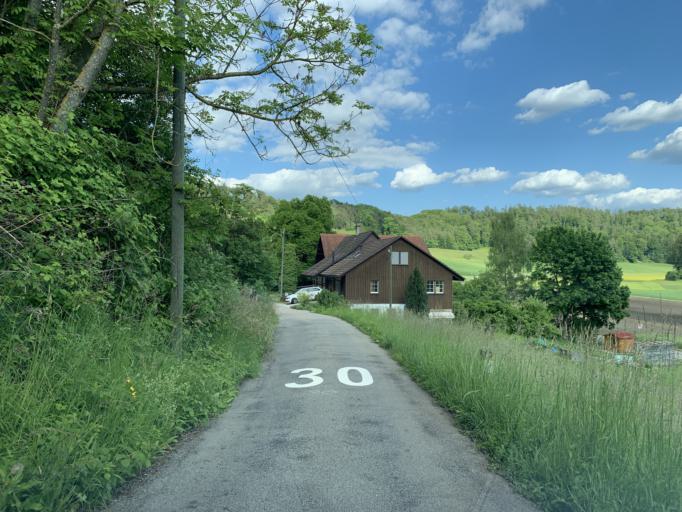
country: CH
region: Zurich
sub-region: Bezirk Winterthur
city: Wuelflingen (Kreis 6) / Niederfeld
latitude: 47.4966
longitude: 8.6783
